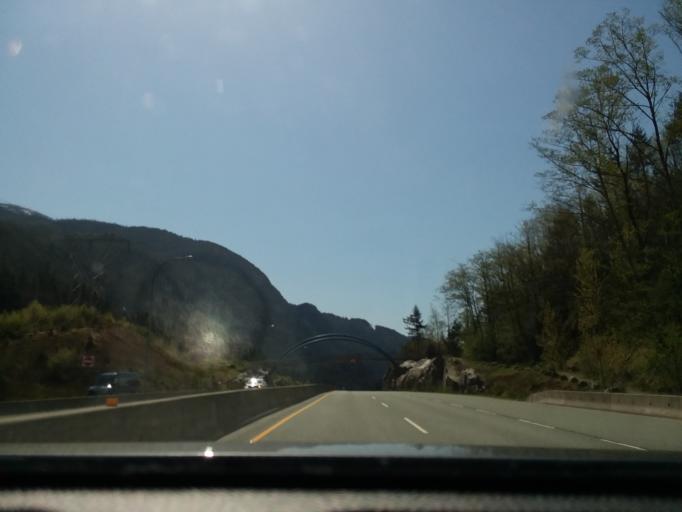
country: CA
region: British Columbia
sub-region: Greater Vancouver Regional District
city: Lions Bay
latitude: 49.6821
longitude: -123.1536
